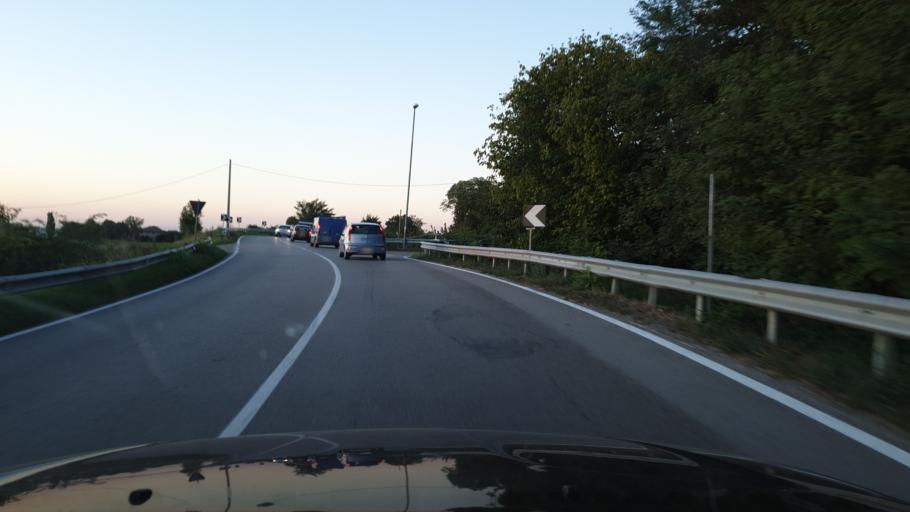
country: IT
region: Emilia-Romagna
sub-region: Provincia di Bologna
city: Ca De Fabbri
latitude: 44.5983
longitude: 11.4382
